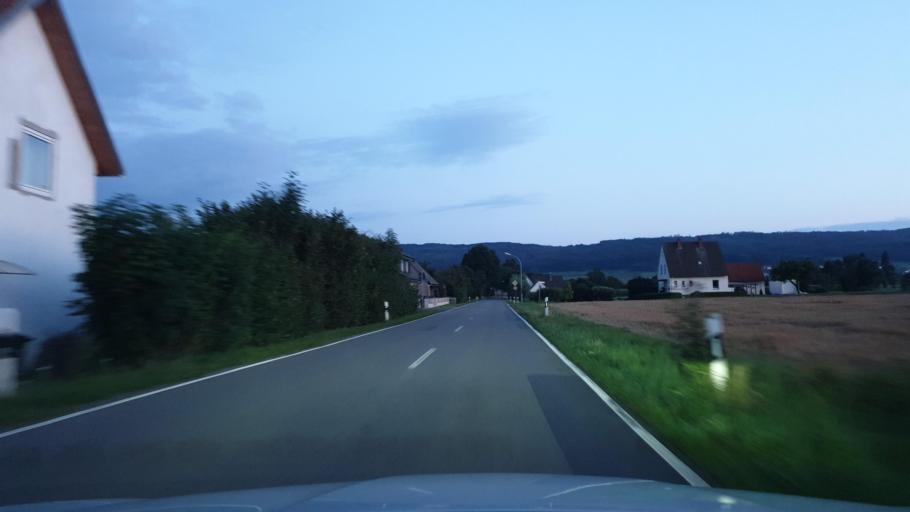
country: DE
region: North Rhine-Westphalia
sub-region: Regierungsbezirk Detmold
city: Huellhorst
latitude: 52.3246
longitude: 8.6679
